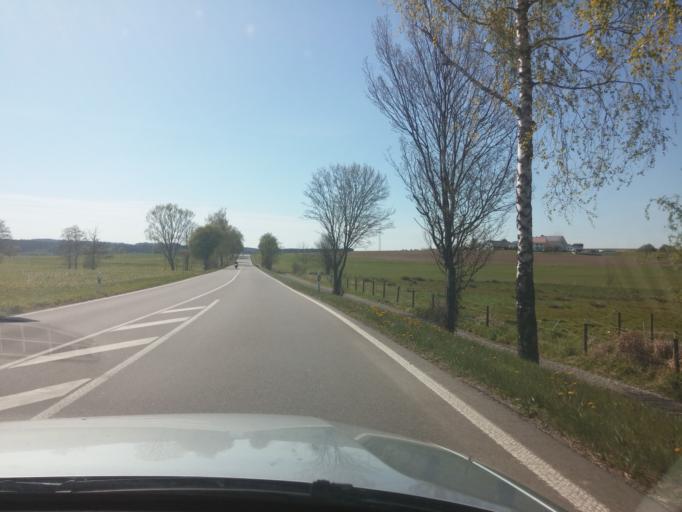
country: DE
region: Baden-Wuerttemberg
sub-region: Tuebingen Region
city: Eberhardzell
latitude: 47.9628
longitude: 9.8328
